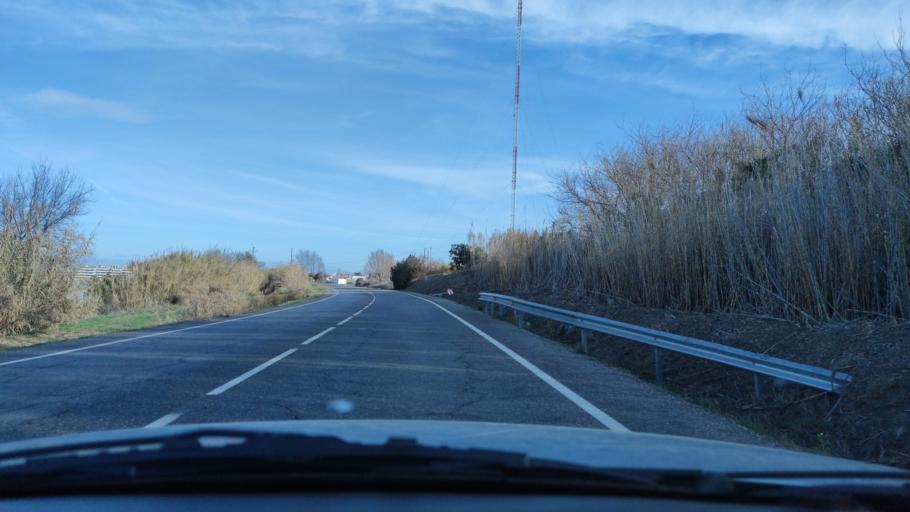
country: ES
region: Catalonia
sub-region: Provincia de Lleida
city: Lleida
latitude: 41.5934
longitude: 0.6342
